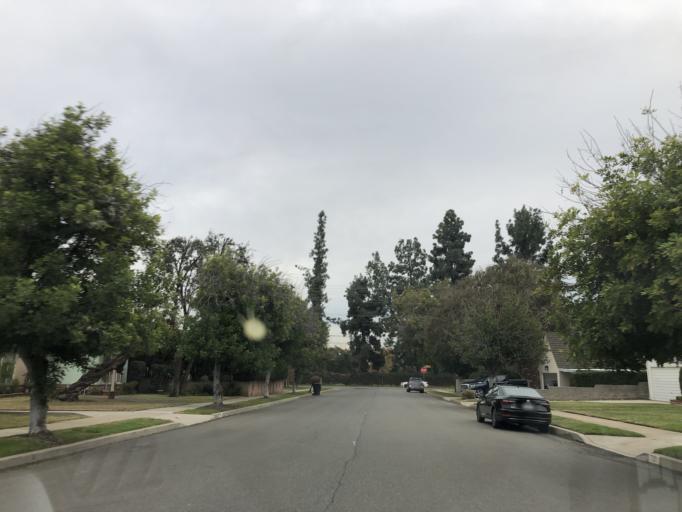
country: US
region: California
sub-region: Los Angeles County
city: San Marino
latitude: 34.1144
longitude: -118.0961
